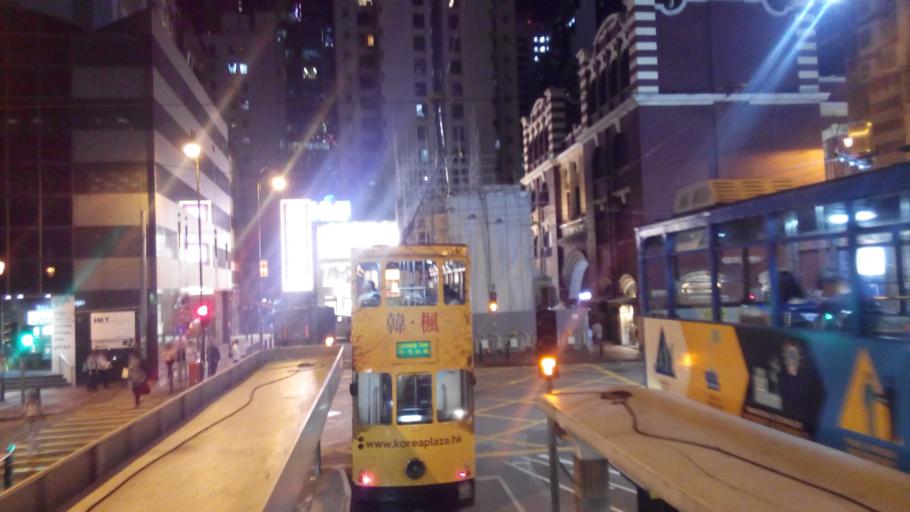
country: HK
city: Hong Kong
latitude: 22.2869
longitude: 114.1509
